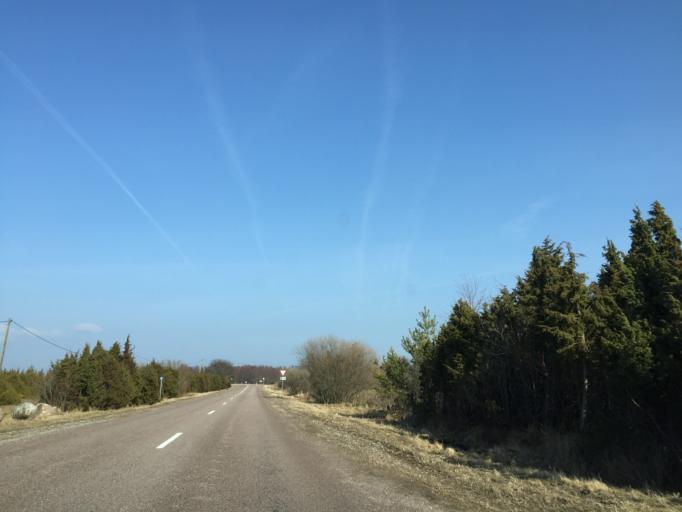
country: EE
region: Saare
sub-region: Kuressaare linn
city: Kuressaare
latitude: 58.0014
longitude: 22.0343
